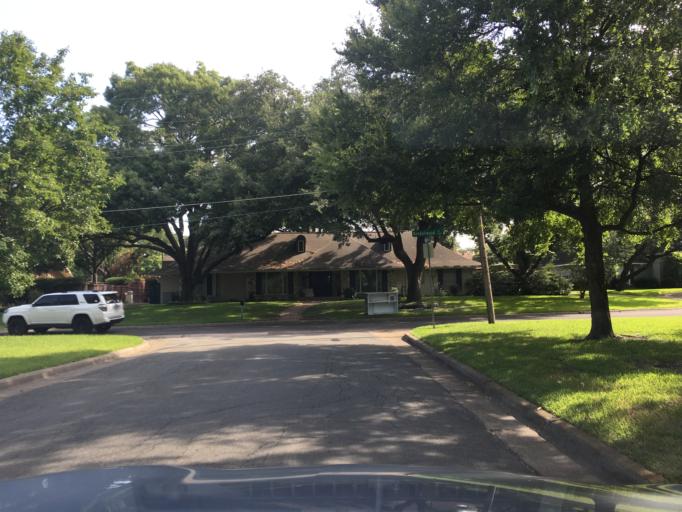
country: US
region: Texas
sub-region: Dallas County
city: Richardson
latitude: 32.9305
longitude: -96.7828
